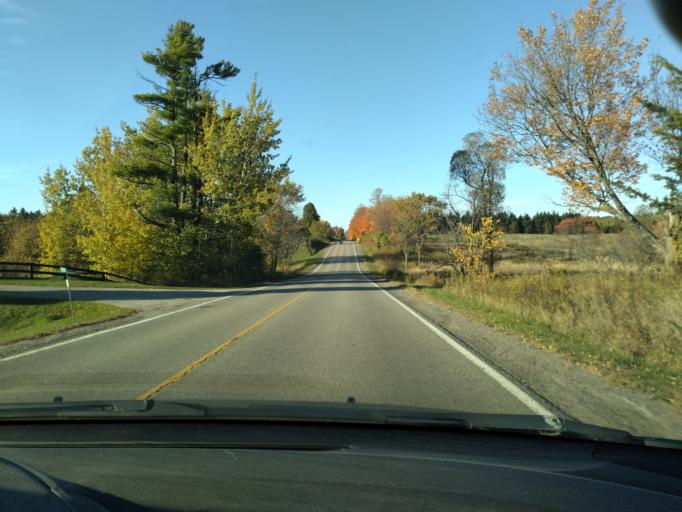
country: CA
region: Ontario
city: Bradford West Gwillimbury
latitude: 43.9541
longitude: -79.7161
